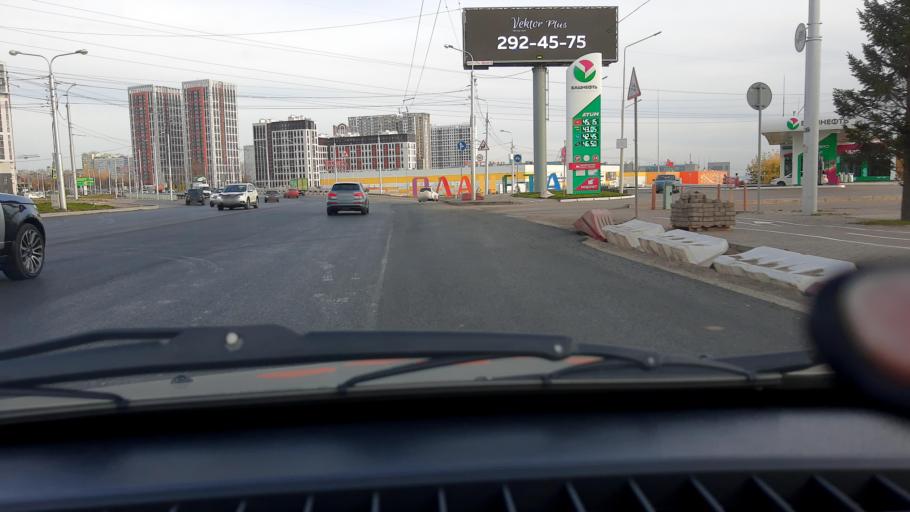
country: RU
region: Bashkortostan
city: Ufa
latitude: 54.7530
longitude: 56.0323
